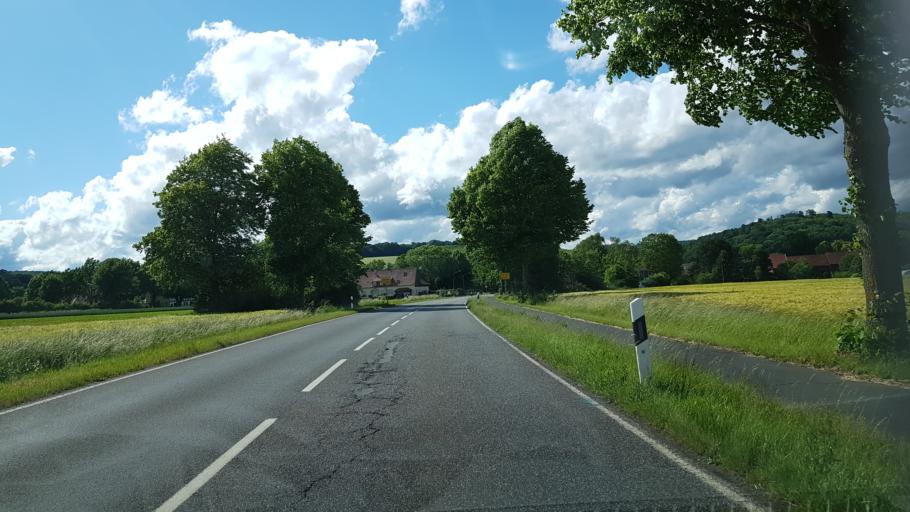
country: DE
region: Lower Saxony
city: Hardegsen
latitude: 51.5959
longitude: 9.8603
